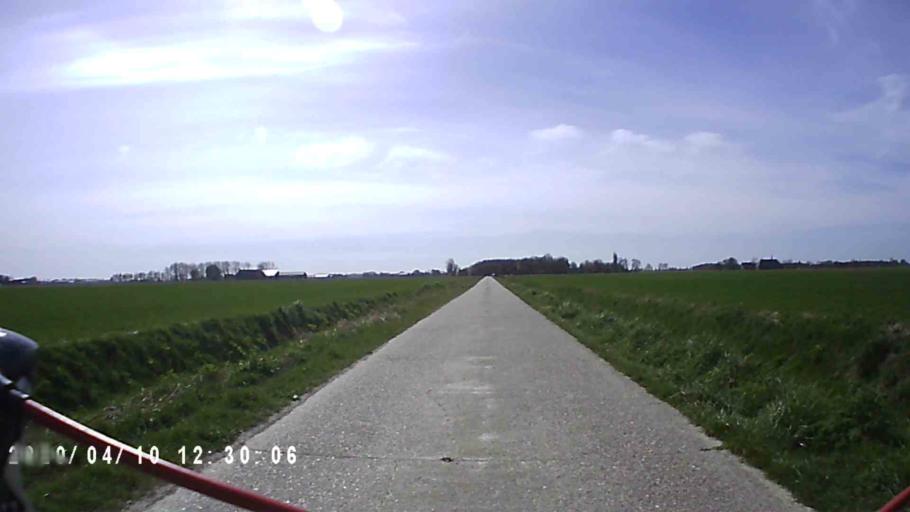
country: NL
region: Groningen
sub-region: Gemeente De Marne
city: Ulrum
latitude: 53.4013
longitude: 6.4101
